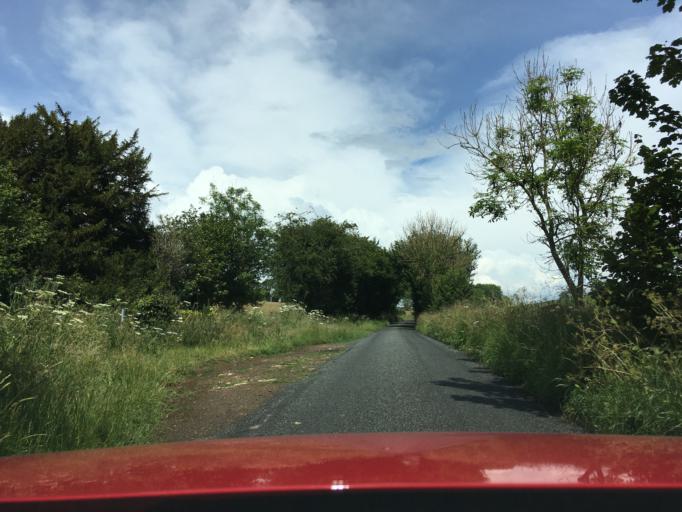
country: GB
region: England
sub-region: Gloucestershire
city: Tetbury
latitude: 51.6220
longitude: -2.2226
